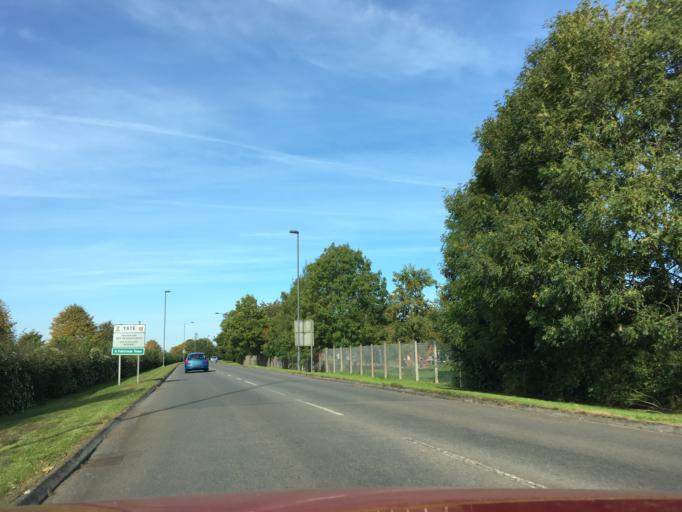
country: GB
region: England
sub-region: South Gloucestershire
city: Yate
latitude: 51.5305
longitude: -2.4325
